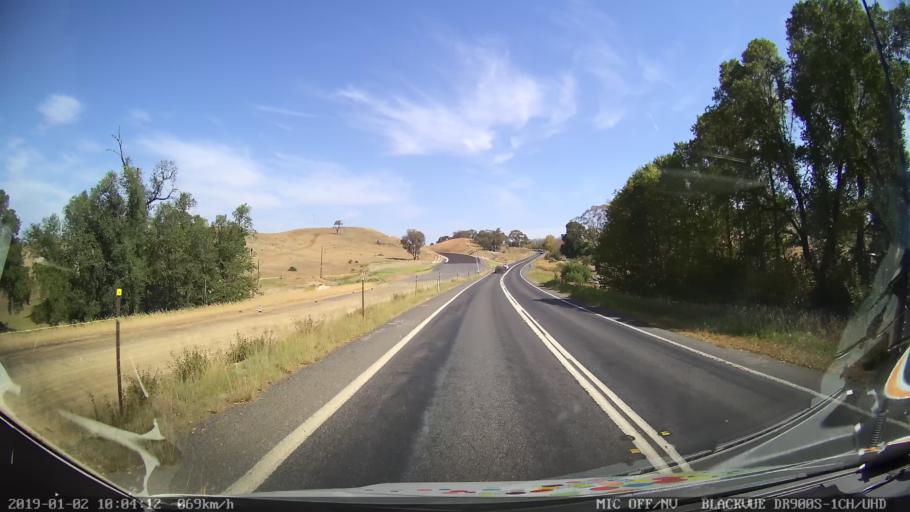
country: AU
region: New South Wales
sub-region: Gundagai
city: Gundagai
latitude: -35.1701
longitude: 148.1237
